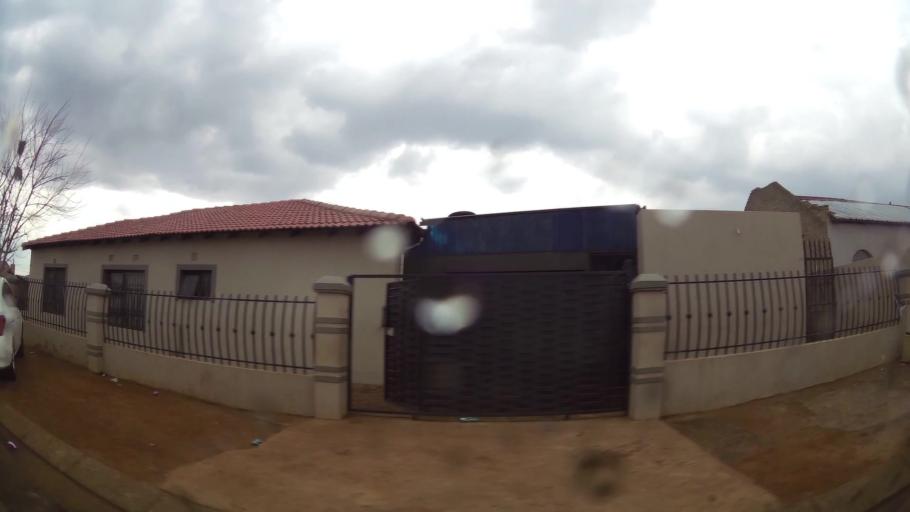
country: ZA
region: Gauteng
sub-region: Ekurhuleni Metropolitan Municipality
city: Germiston
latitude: -26.3601
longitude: 28.1642
